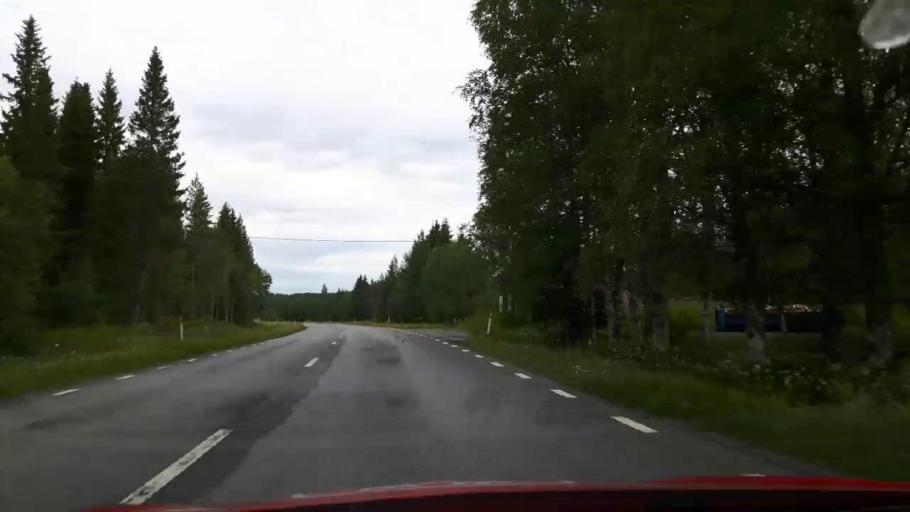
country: SE
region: Jaemtland
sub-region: Stroemsunds Kommun
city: Stroemsund
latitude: 63.5539
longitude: 15.3733
